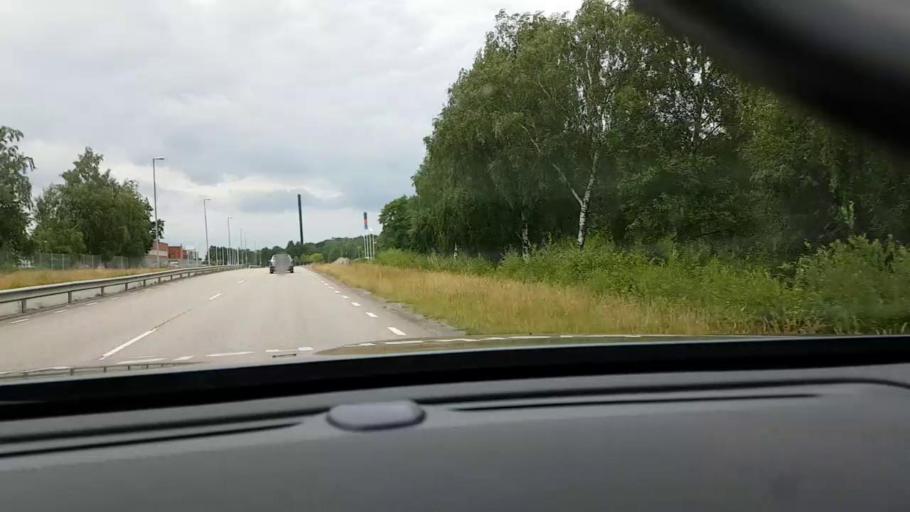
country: SE
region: Skane
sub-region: Hassleholms Kommun
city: Hassleholm
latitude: 56.1579
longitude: 13.8087
